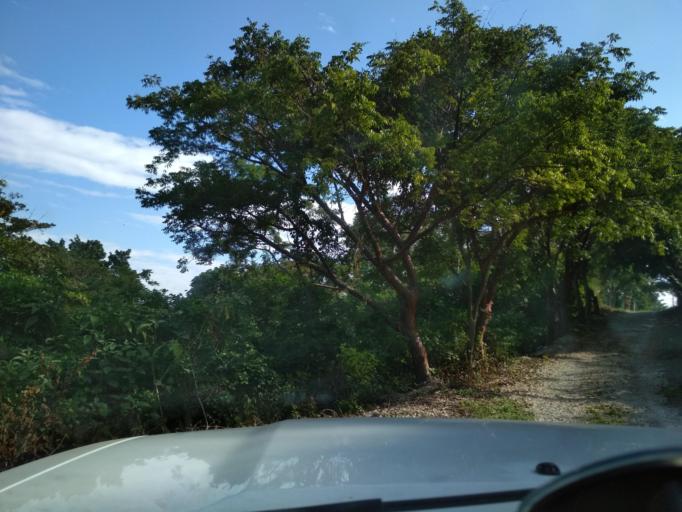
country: MX
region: Veracruz
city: Rinconada
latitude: 19.3565
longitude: -96.5601
